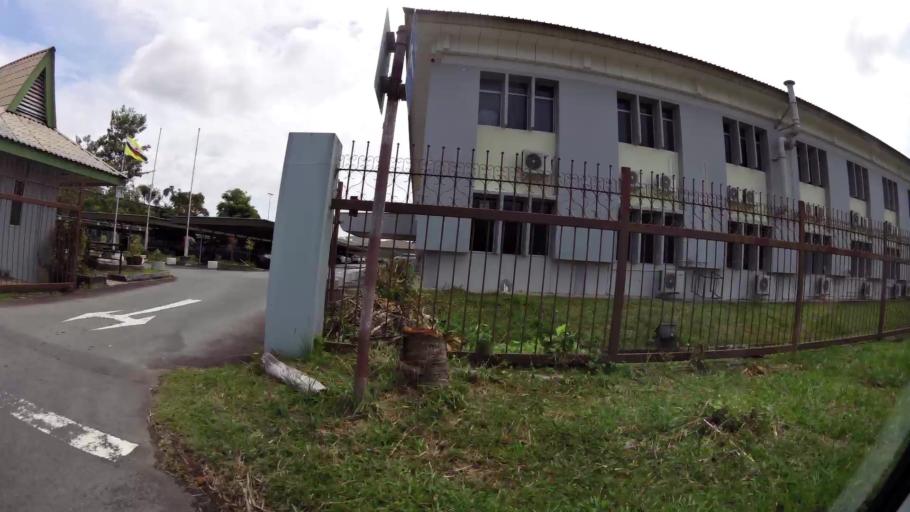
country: BN
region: Brunei and Muara
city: Bandar Seri Begawan
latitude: 4.9062
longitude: 114.9110
